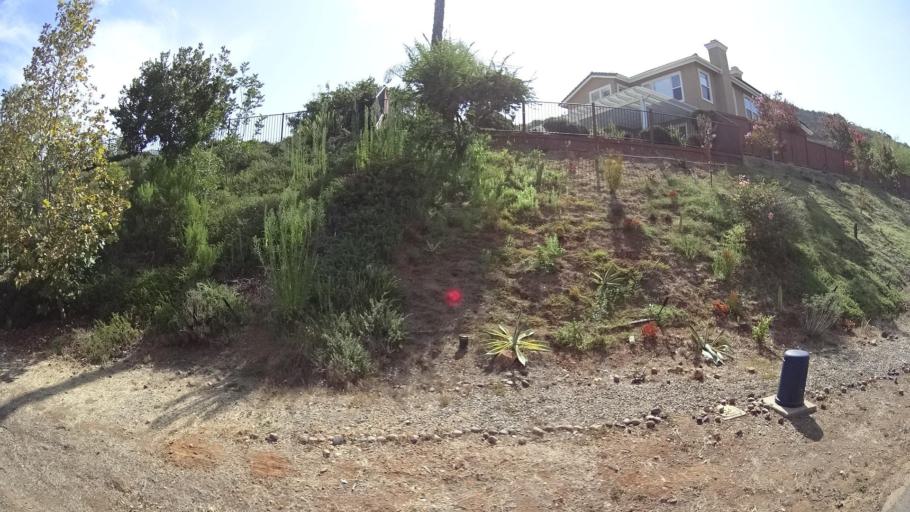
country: US
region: California
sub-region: San Diego County
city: San Marcos
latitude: 33.1689
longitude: -117.1457
